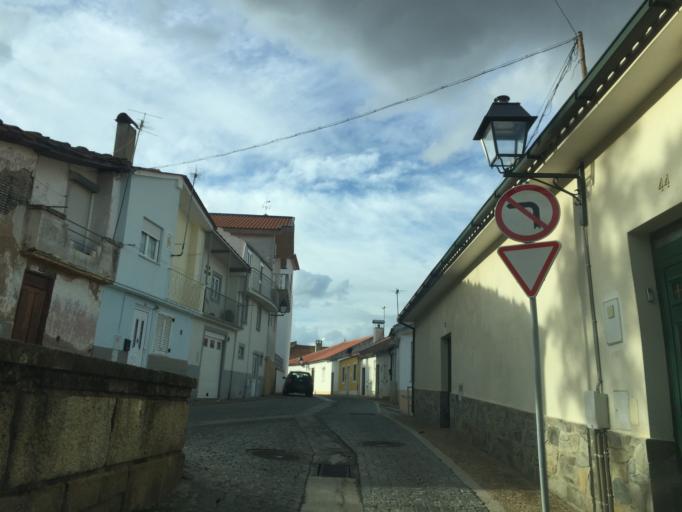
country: PT
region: Braganca
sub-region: Alfandega da Fe
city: Alfandega da Fe
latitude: 41.3414
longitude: -6.9653
